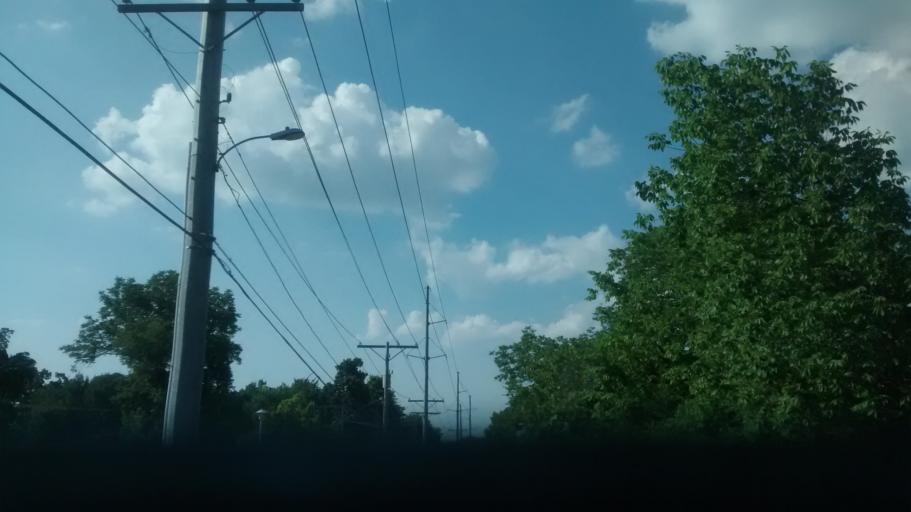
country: US
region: Arkansas
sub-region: Washington County
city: Fayetteville
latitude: 36.0708
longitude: -94.1674
